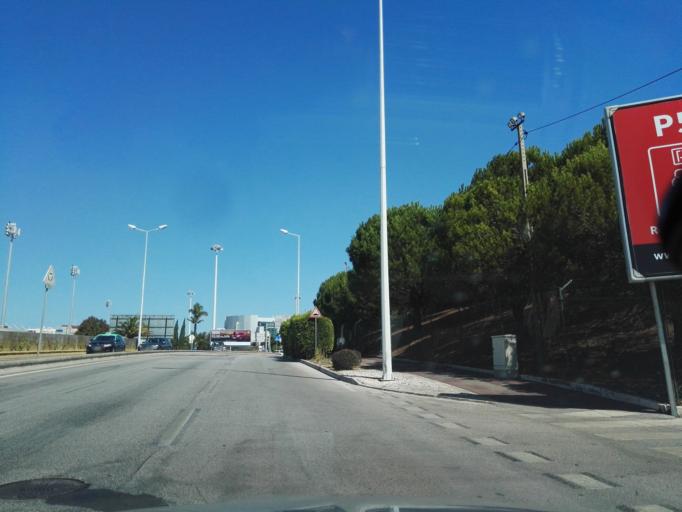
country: PT
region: Lisbon
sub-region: Loures
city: Moscavide
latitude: 38.7658
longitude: -9.1291
